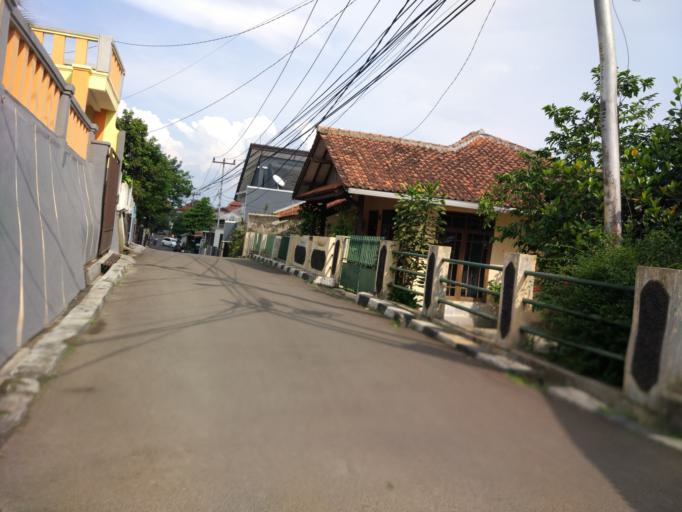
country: ID
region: West Java
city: Bandung
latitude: -6.9036
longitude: 107.6897
